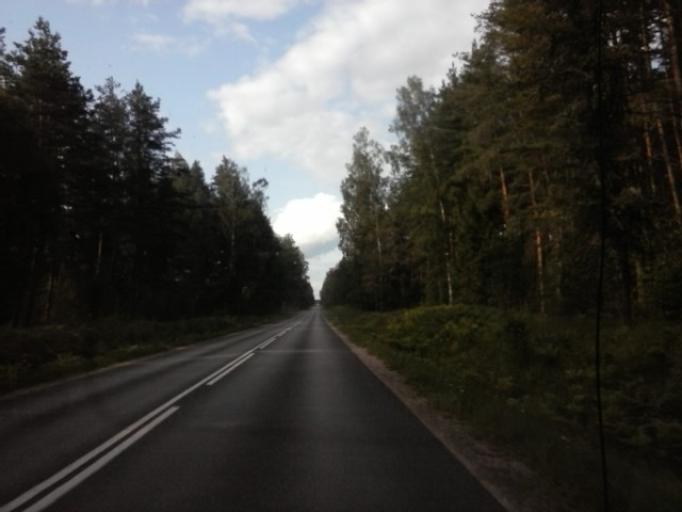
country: LV
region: Valmieras Rajons
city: Valmiera
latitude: 57.4929
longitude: 25.4144
